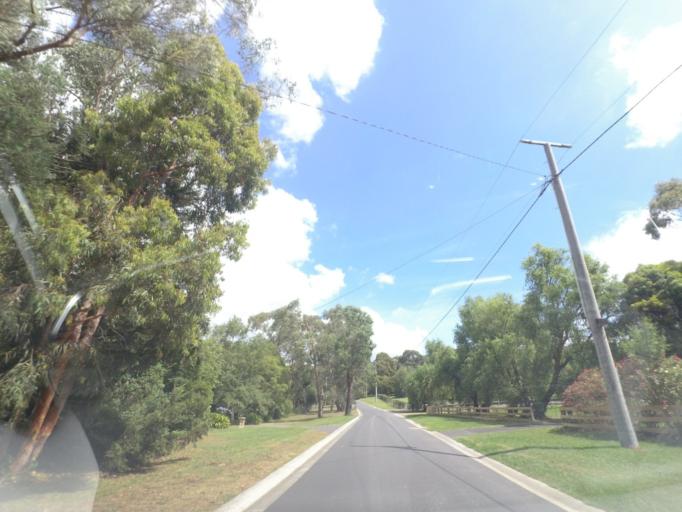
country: AU
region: Victoria
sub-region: Yarra Ranges
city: Mount Evelyn
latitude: -37.7804
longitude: 145.3588
